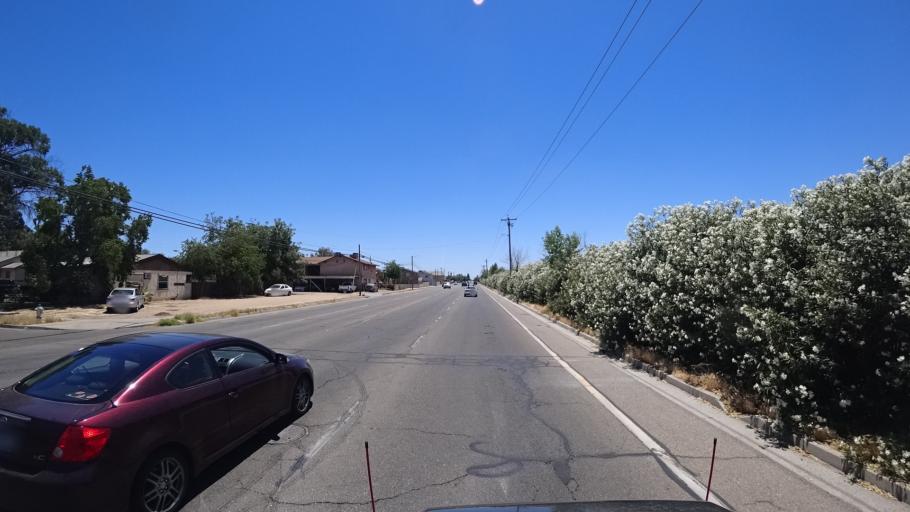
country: US
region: California
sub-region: Fresno County
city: Fresno
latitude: 36.7325
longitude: -119.7456
